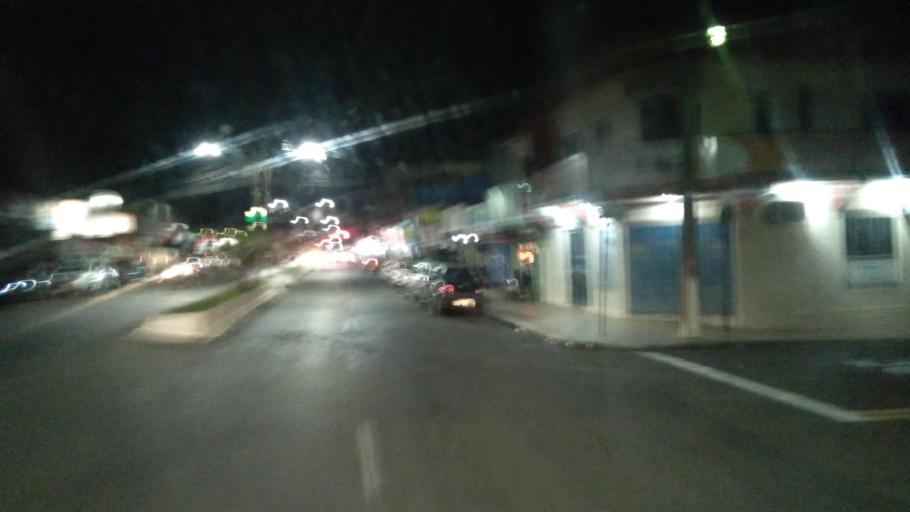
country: BR
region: Goias
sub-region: Mineiros
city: Mineiros
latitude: -17.5634
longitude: -52.5523
